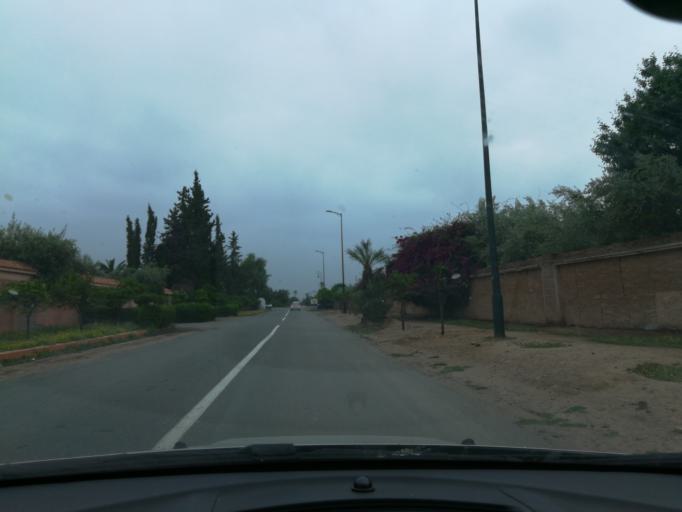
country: MA
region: Marrakech-Tensift-Al Haouz
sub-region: Marrakech
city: Marrakesh
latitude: 31.6481
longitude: -7.9730
